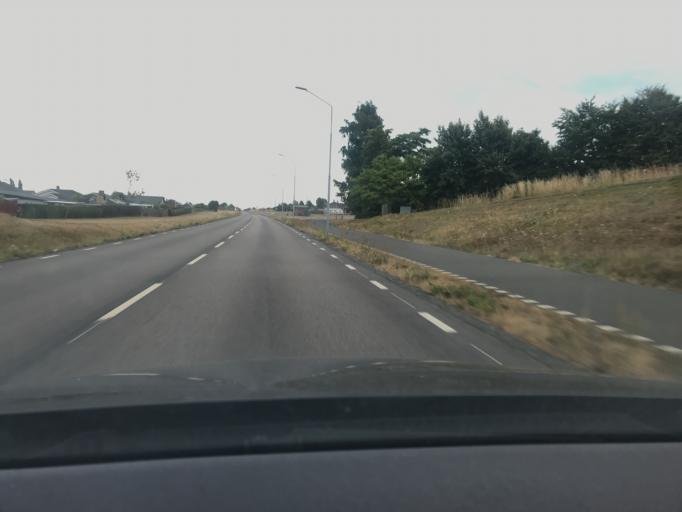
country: SE
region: Skane
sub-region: Simrishamns Kommun
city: Simrishamn
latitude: 55.5477
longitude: 14.3503
